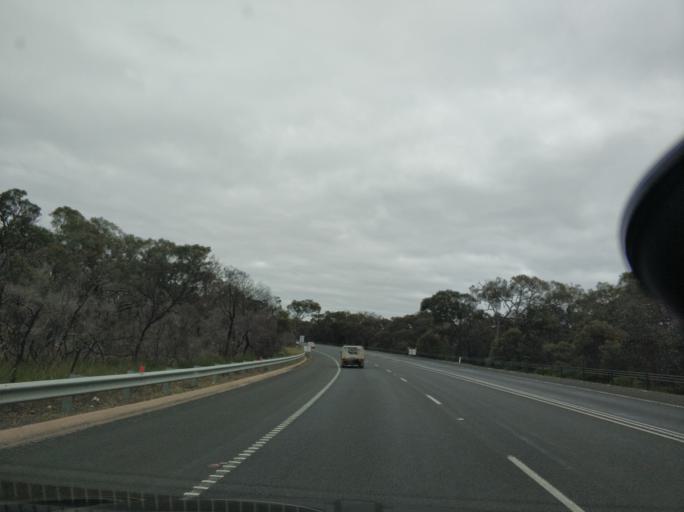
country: AU
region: Victoria
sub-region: Surf Coast
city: Anglesea
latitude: -38.3725
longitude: 144.2301
